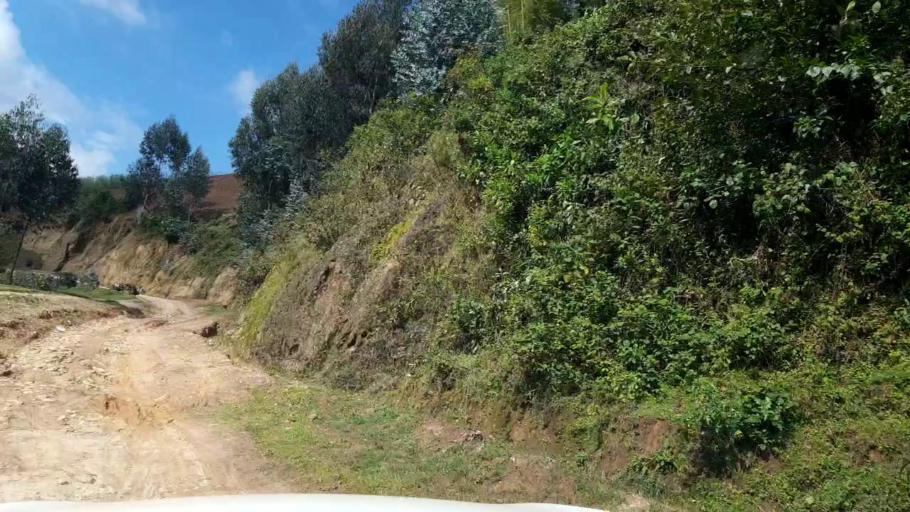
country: RW
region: Western Province
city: Kibuye
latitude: -1.8813
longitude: 29.4719
